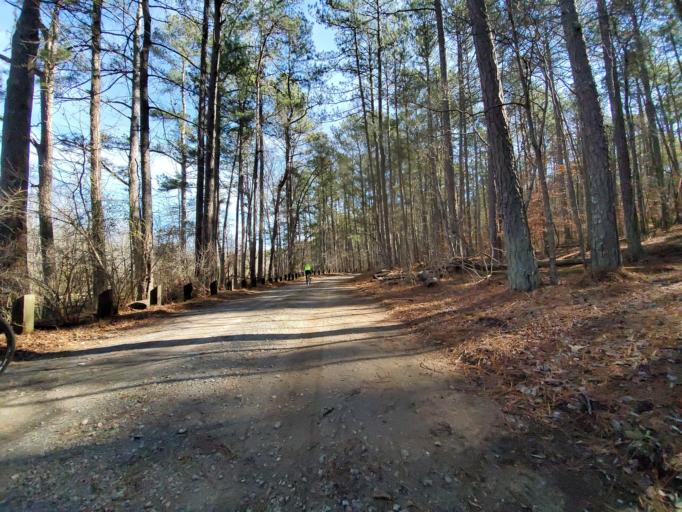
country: US
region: Georgia
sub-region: Fulton County
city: Chattahoochee Hills
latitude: 33.5720
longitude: -84.7213
